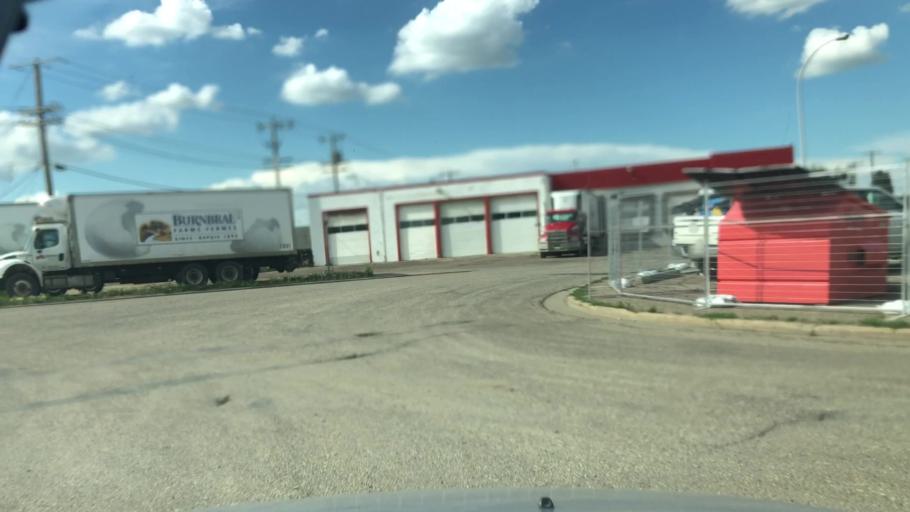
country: CA
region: Alberta
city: Edmonton
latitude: 53.5817
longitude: -113.4508
